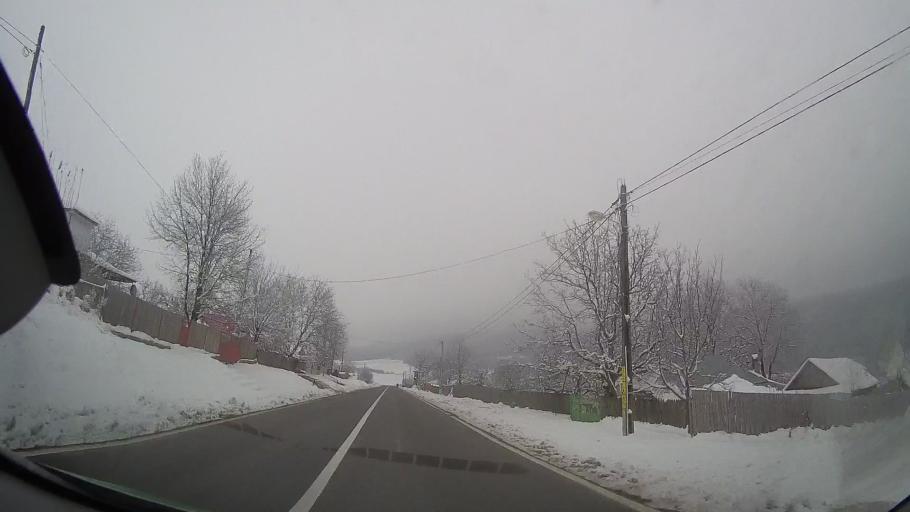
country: RO
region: Neamt
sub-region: Comuna Poenari
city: Poienari
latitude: 46.8764
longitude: 27.1344
